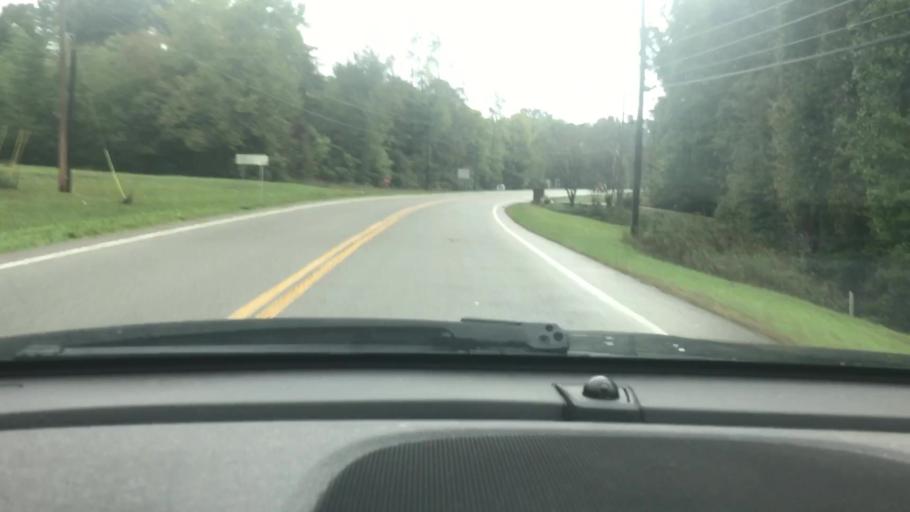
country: US
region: Tennessee
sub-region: Dickson County
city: White Bluff
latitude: 36.1087
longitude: -87.1749
